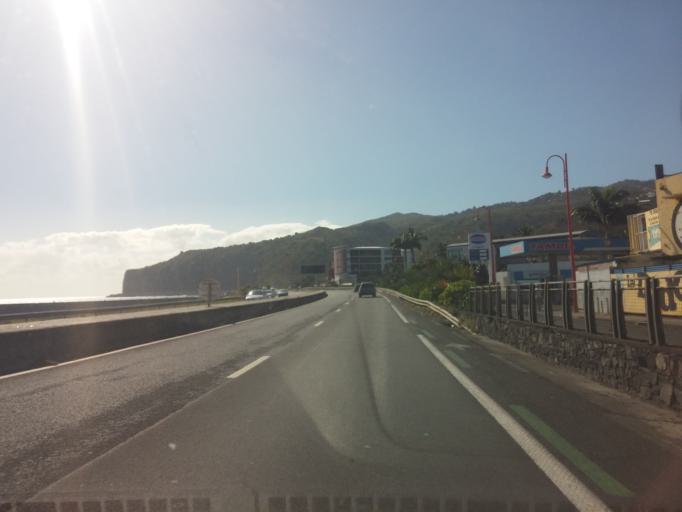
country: RE
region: Reunion
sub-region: Reunion
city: La Possession
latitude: -20.9259
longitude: 55.3362
